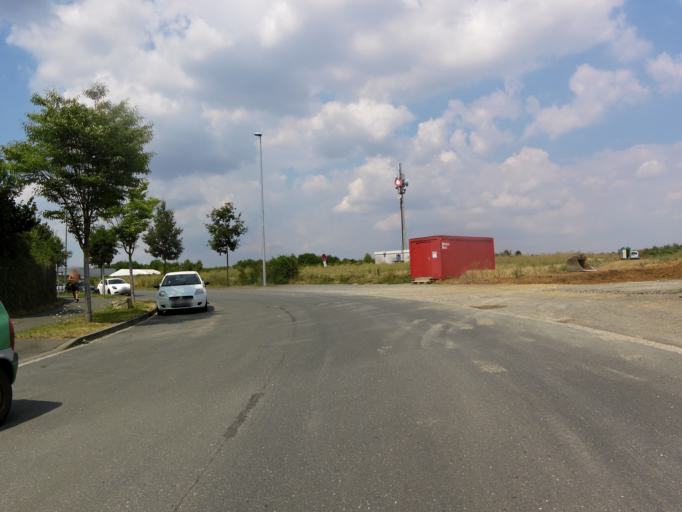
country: DE
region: Bavaria
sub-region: Regierungsbezirk Unterfranken
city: Eibelstadt
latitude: 49.7332
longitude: 9.9728
